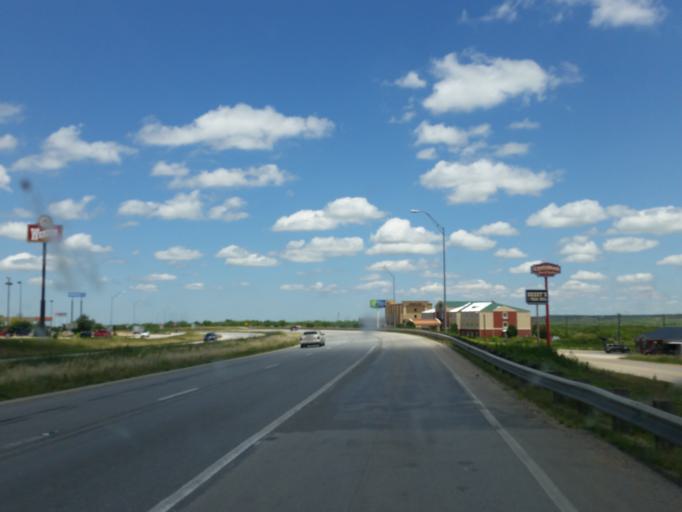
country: US
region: Texas
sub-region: Nolan County
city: Sweetwater
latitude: 32.4505
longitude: -100.3955
